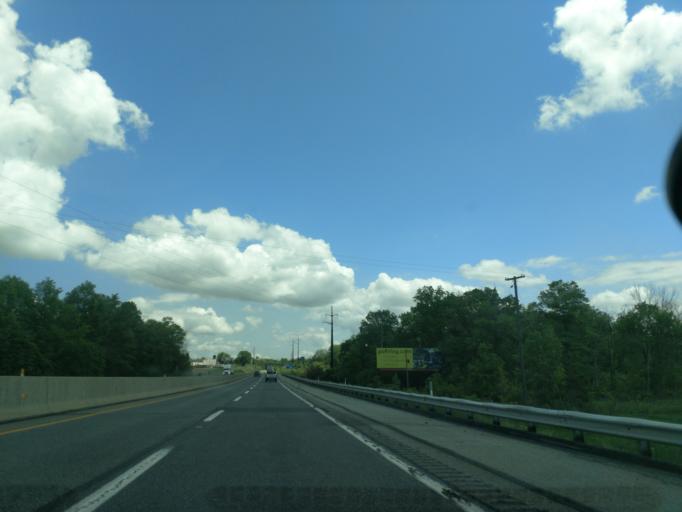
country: US
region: Pennsylvania
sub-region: Lancaster County
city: Reamstown
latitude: 40.2255
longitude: -76.1042
